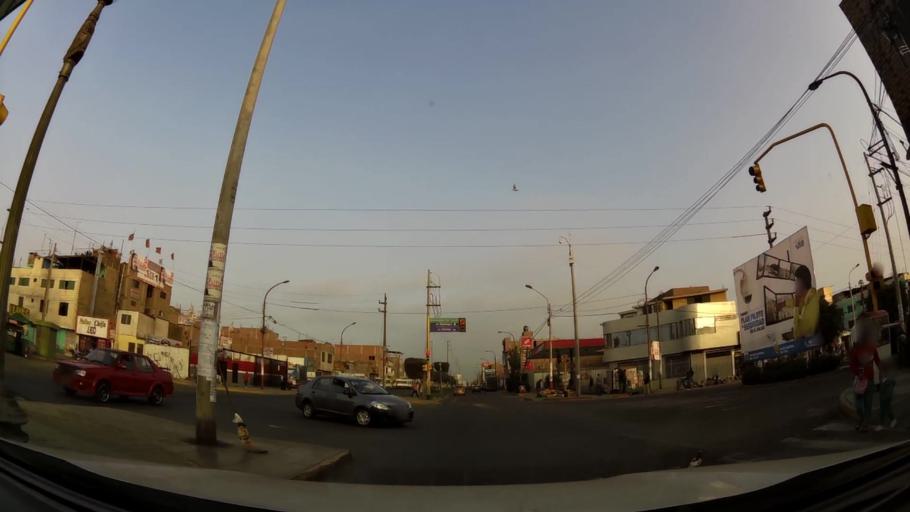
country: PE
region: Callao
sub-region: Callao
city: Callao
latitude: -12.0011
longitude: -77.1063
